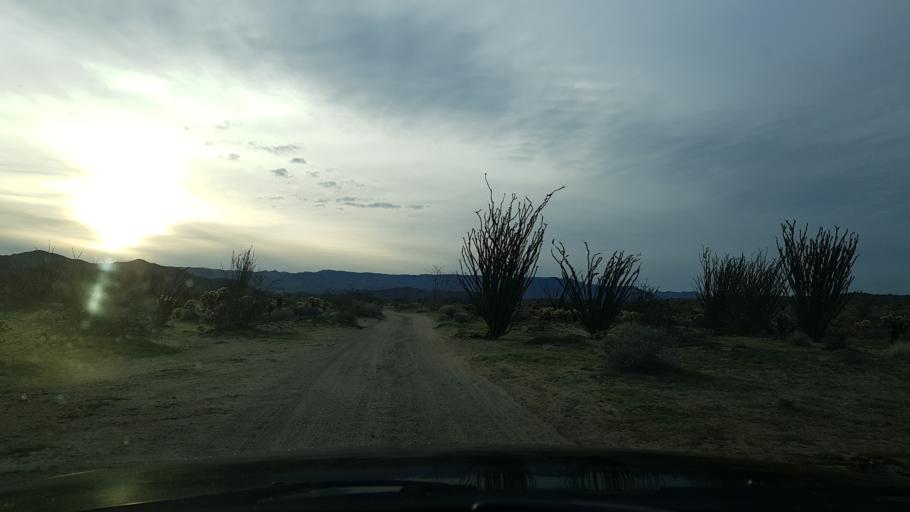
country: MX
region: Baja California
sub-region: Tecate
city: Cereso del Hongo
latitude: 32.8135
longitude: -116.1403
